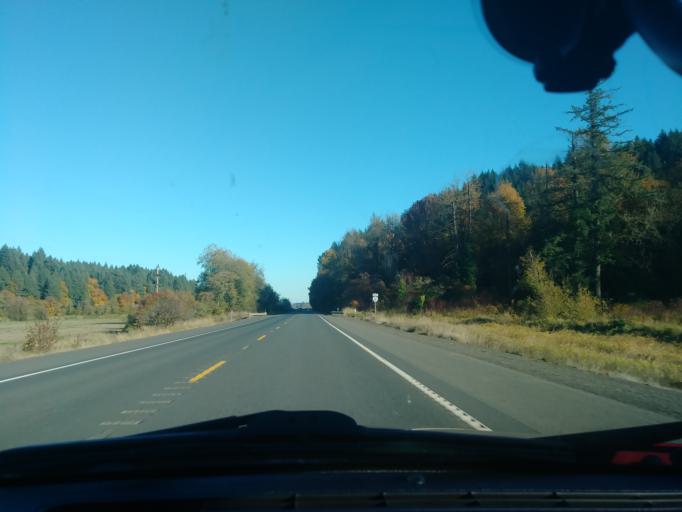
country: US
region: Oregon
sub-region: Washington County
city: Banks
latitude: 45.6151
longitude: -123.1820
